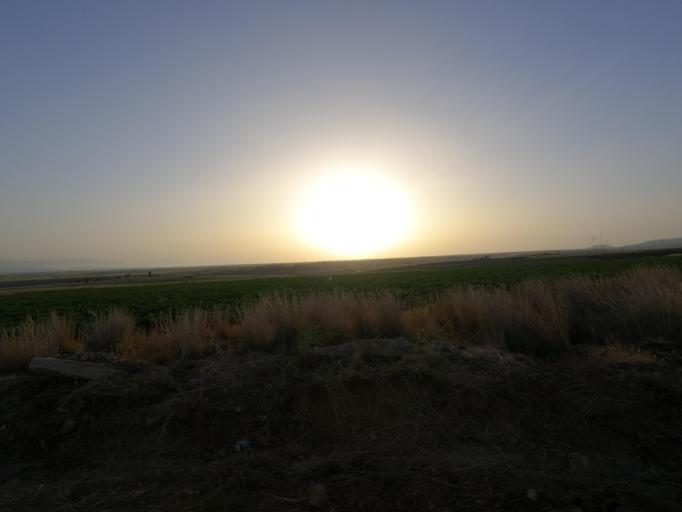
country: CY
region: Lefkosia
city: Astromeritis
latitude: 35.1073
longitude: 33.0148
